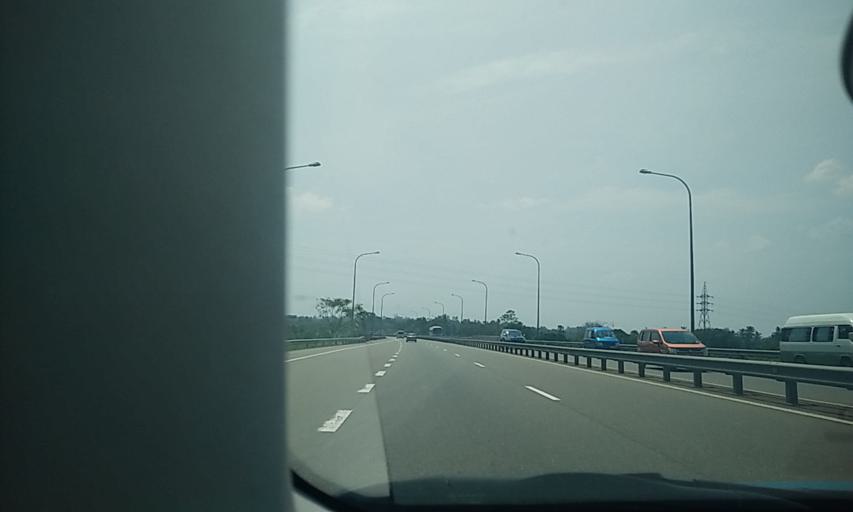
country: LK
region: Western
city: Homagama
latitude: 6.7785
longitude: 79.9802
